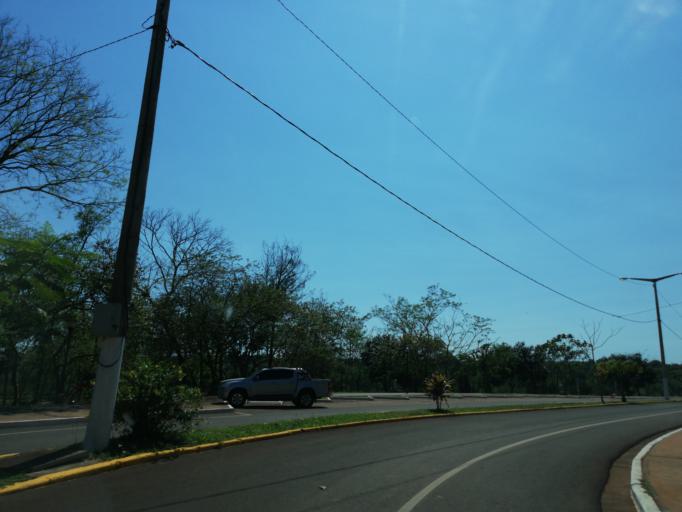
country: AR
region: Misiones
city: Puerto Eldorado
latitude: -26.4084
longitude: -54.6934
